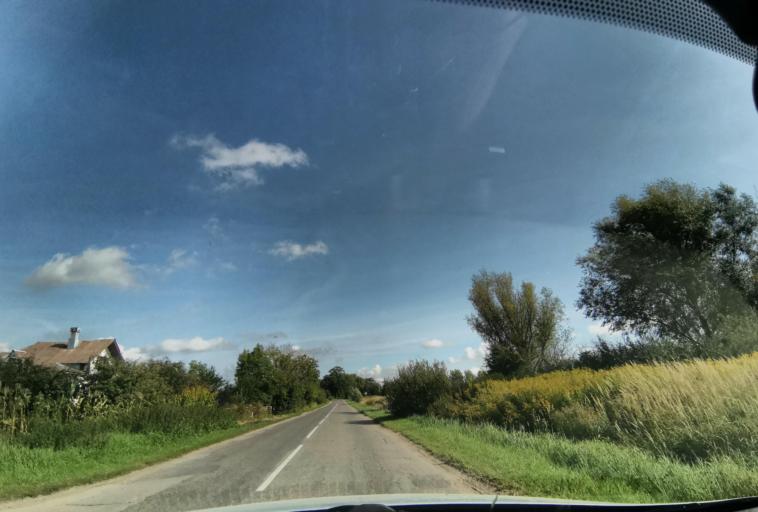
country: RU
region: Kaliningrad
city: Chernyakhovsk
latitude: 54.6514
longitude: 21.8462
